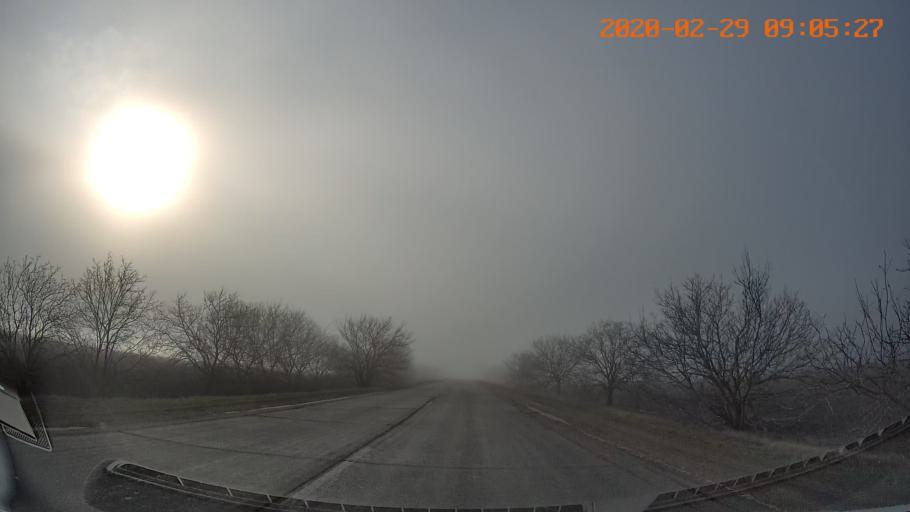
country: MD
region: Telenesti
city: Tiraspolul Nou
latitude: 46.8891
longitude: 29.7403
